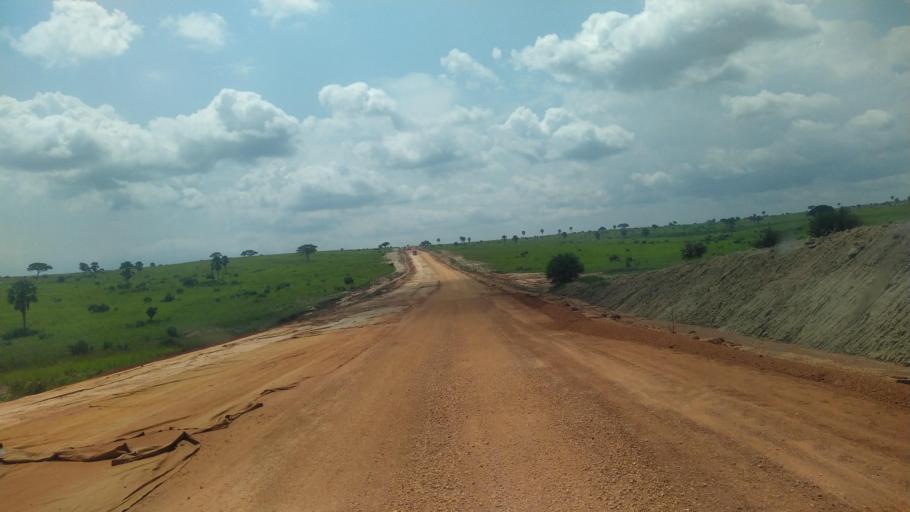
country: UG
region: Western Region
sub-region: Bulisa District
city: Bulisa
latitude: 2.3330
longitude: 31.5671
